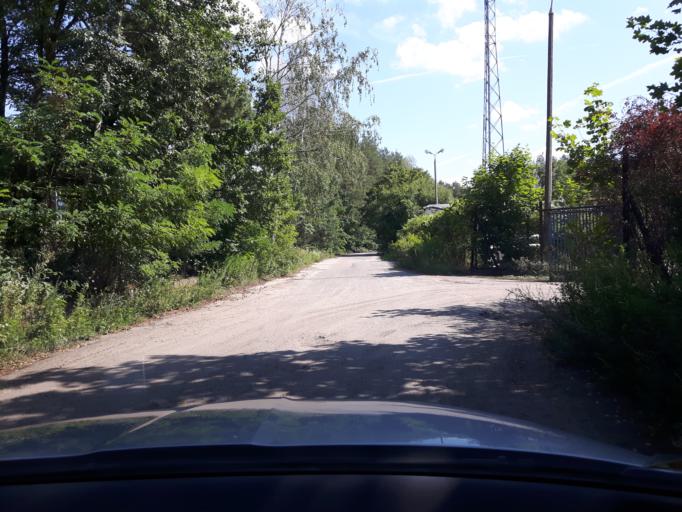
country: PL
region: Masovian Voivodeship
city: Zielonka
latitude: 52.2904
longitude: 21.1547
